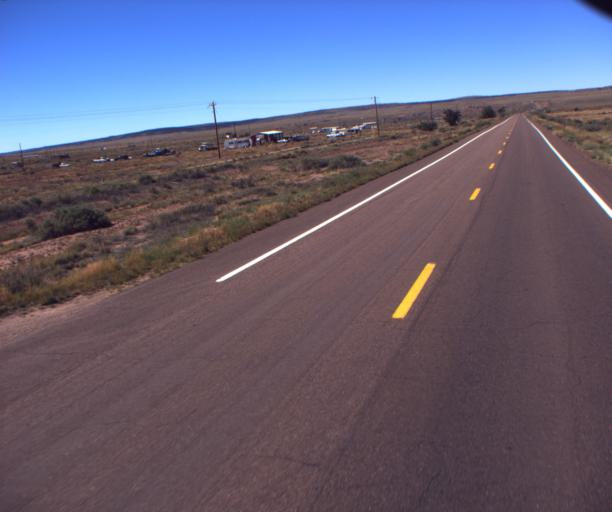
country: US
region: Arizona
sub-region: Apache County
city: Saint Johns
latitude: 34.5075
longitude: -109.4247
